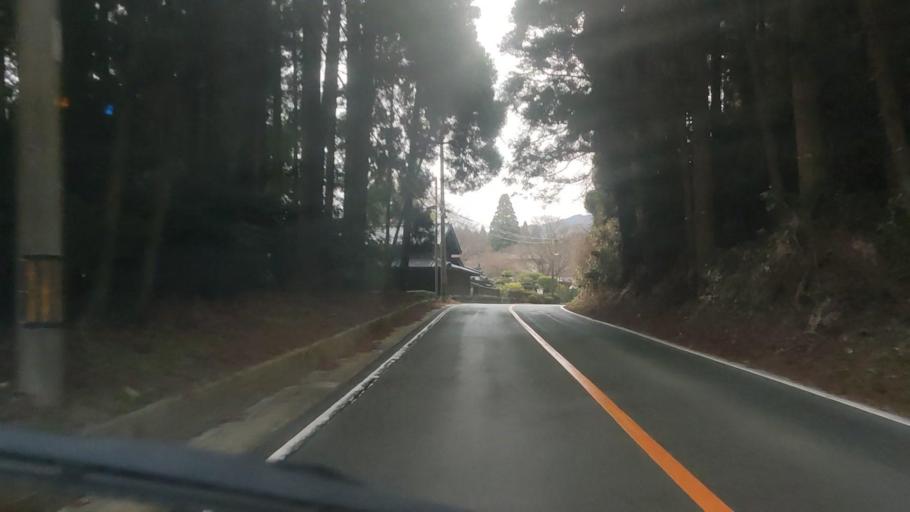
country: JP
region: Kumamoto
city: Aso
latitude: 32.8556
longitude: 131.1561
